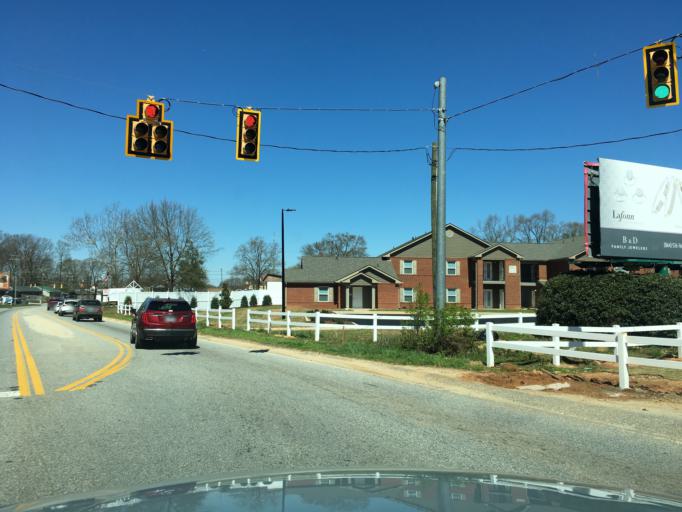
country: US
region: South Carolina
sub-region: Spartanburg County
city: Fairforest
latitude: 34.9312
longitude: -82.0009
